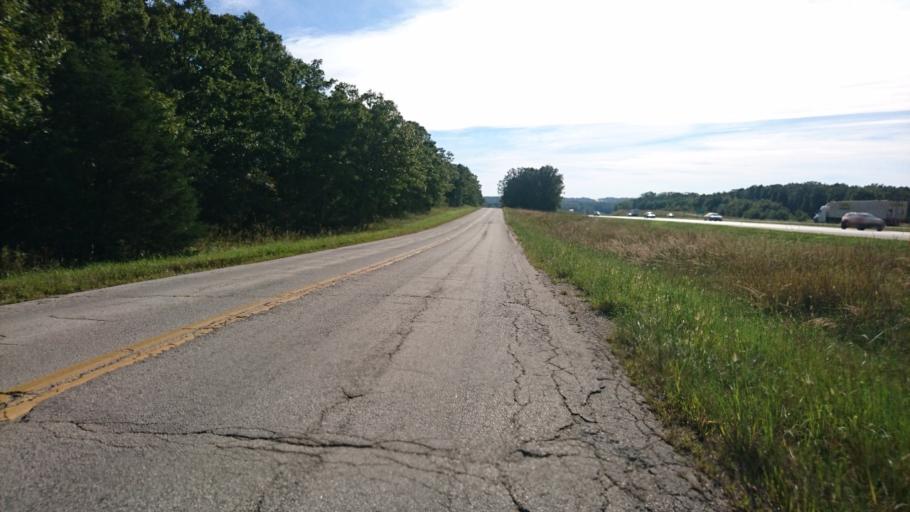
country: US
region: Missouri
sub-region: Crawford County
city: Cuba
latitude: 38.1129
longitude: -91.3289
